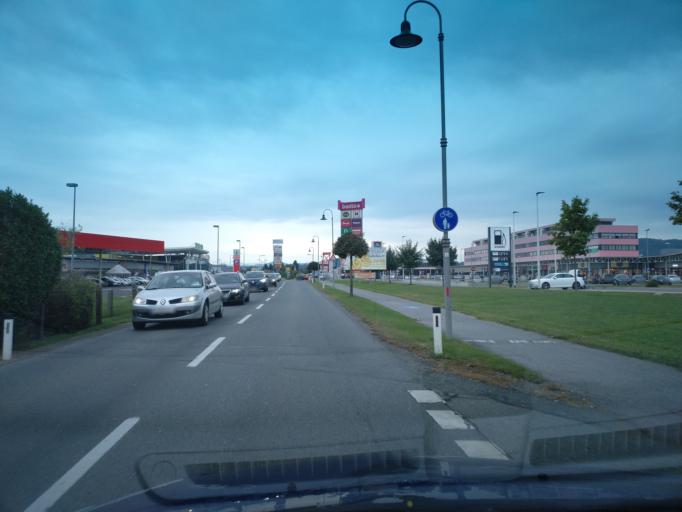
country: AT
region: Styria
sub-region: Politischer Bezirk Leibnitz
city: Kaindorf an der Sulm
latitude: 46.7971
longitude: 15.5579
